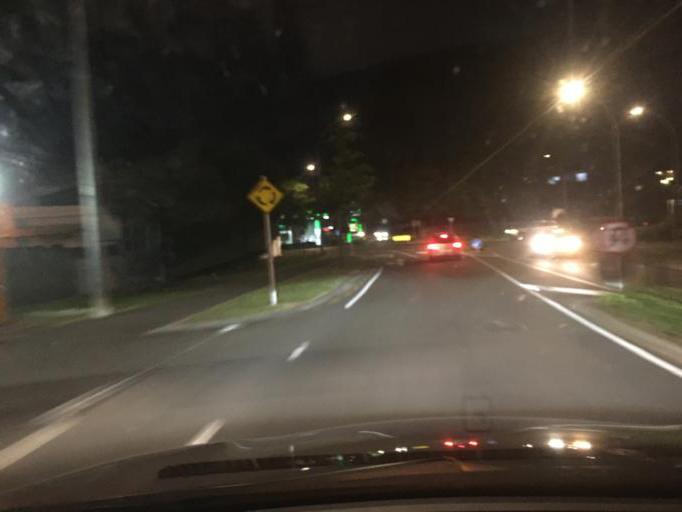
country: NZ
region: Waikato
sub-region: Hamilton City
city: Hamilton
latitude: -37.7905
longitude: 175.2791
